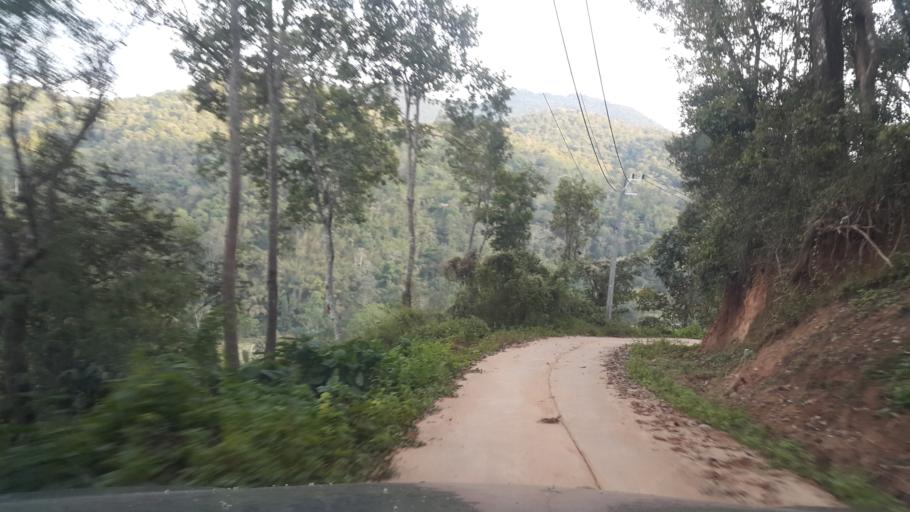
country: TH
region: Chiang Mai
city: Samoeng
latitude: 19.0090
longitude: 98.6690
